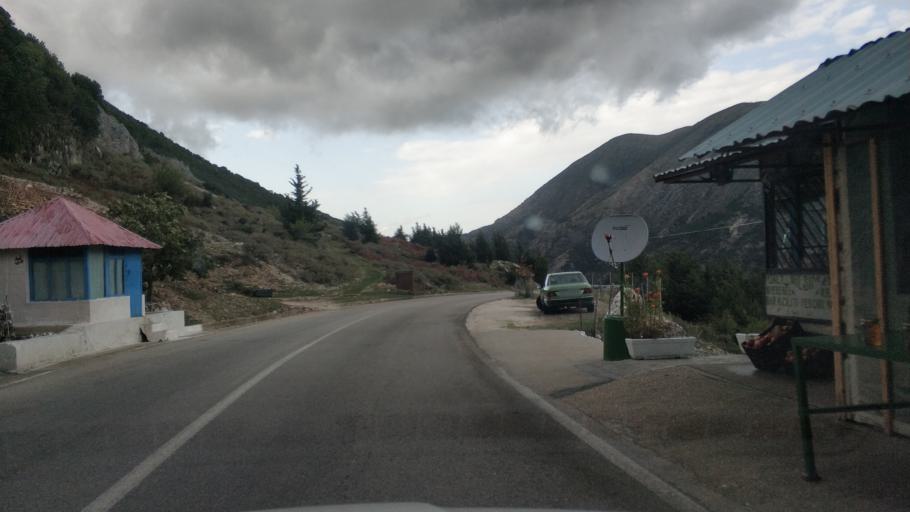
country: AL
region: Vlore
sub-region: Rrethi i Vlores
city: Orikum
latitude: 40.2381
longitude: 19.5519
